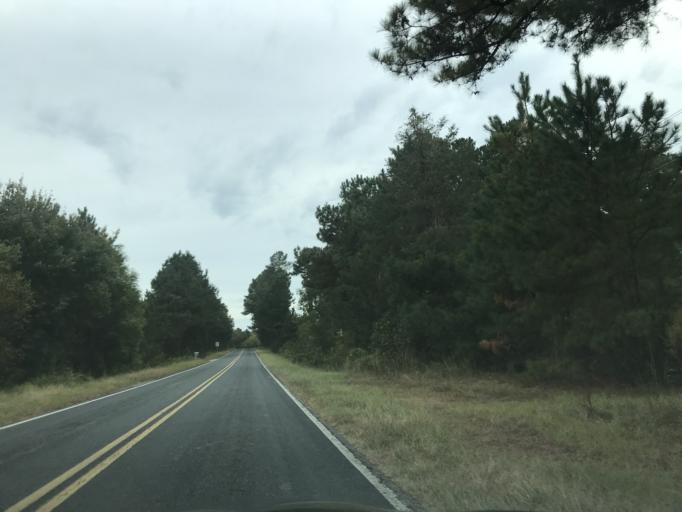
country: US
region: North Carolina
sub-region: Wake County
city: Knightdale
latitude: 35.8228
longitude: -78.4867
